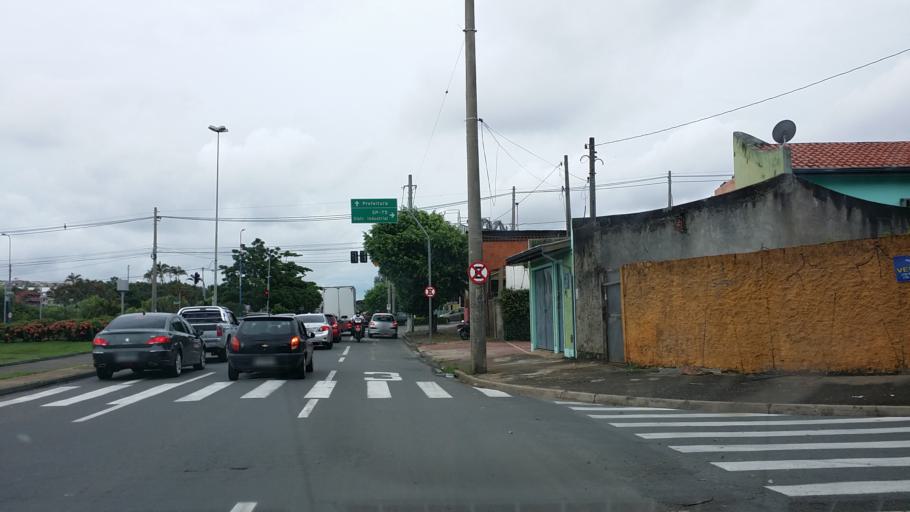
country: BR
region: Sao Paulo
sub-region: Indaiatuba
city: Indaiatuba
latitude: -23.1189
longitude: -47.2321
